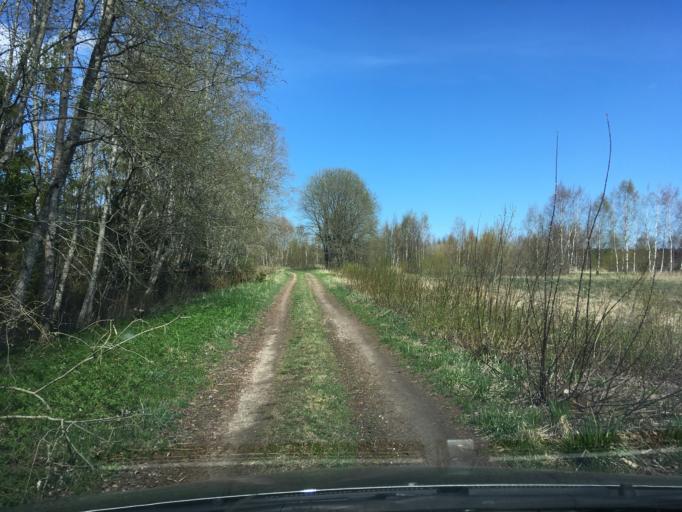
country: EE
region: Harju
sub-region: Raasiku vald
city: Arukula
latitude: 59.2064
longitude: 25.1208
